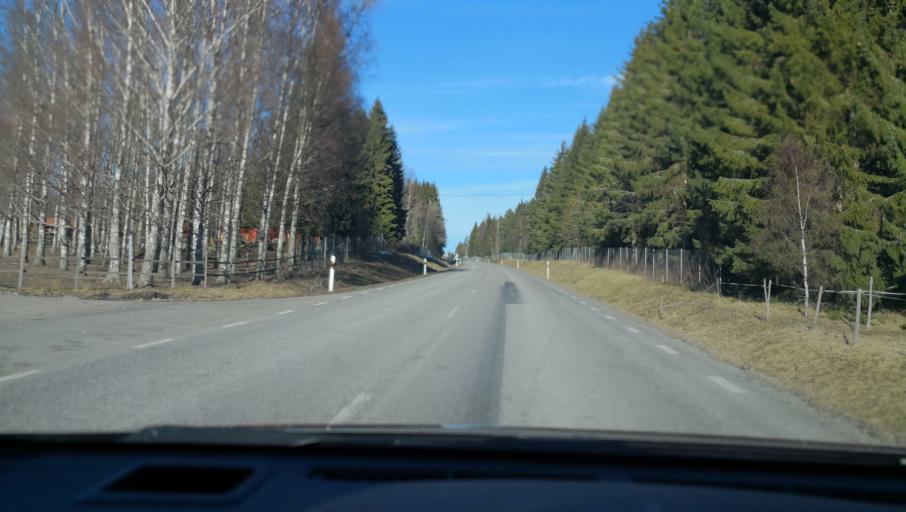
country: SE
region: Uppsala
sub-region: Uppsala Kommun
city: Vattholma
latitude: 60.0294
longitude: 17.7500
